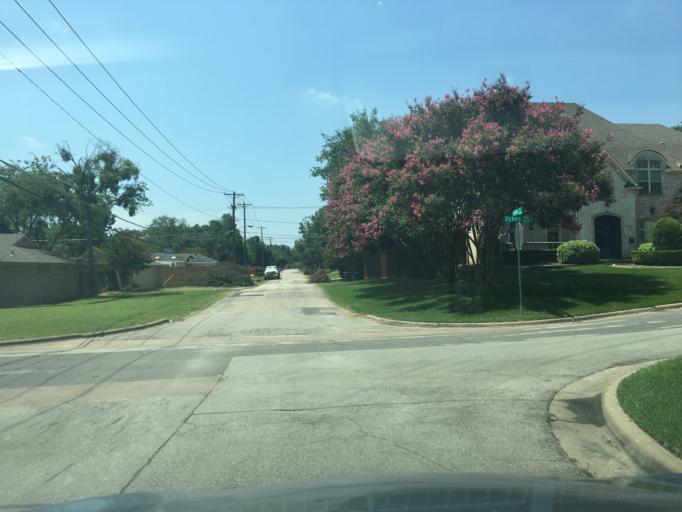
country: US
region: Texas
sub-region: Dallas County
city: Addison
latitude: 32.9211
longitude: -96.7973
